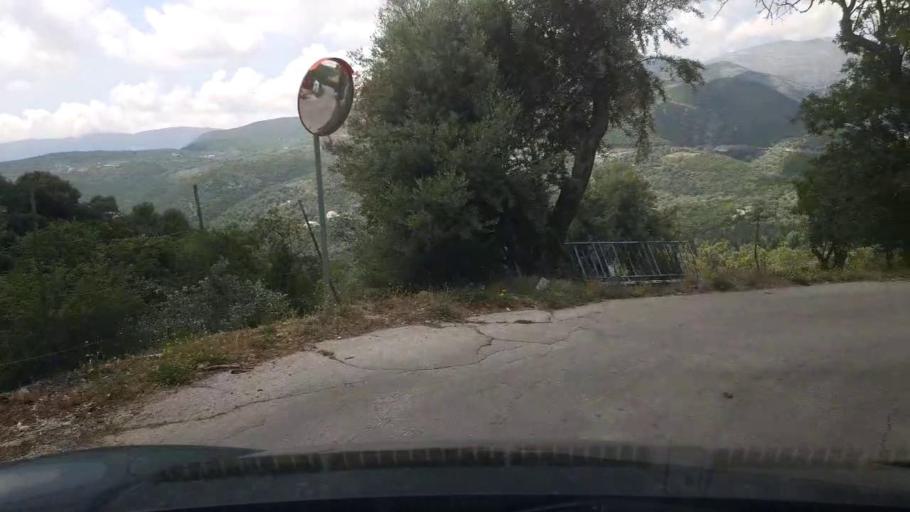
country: GR
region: Ionian Islands
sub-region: Lefkada
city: Nidri
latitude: 38.6424
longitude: 20.7054
